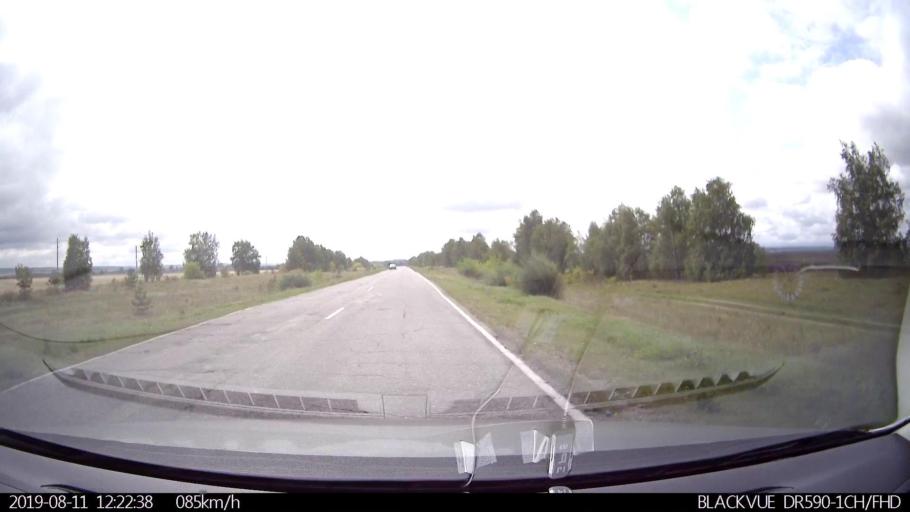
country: RU
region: Ulyanovsk
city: Ignatovka
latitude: 53.9053
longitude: 47.9513
